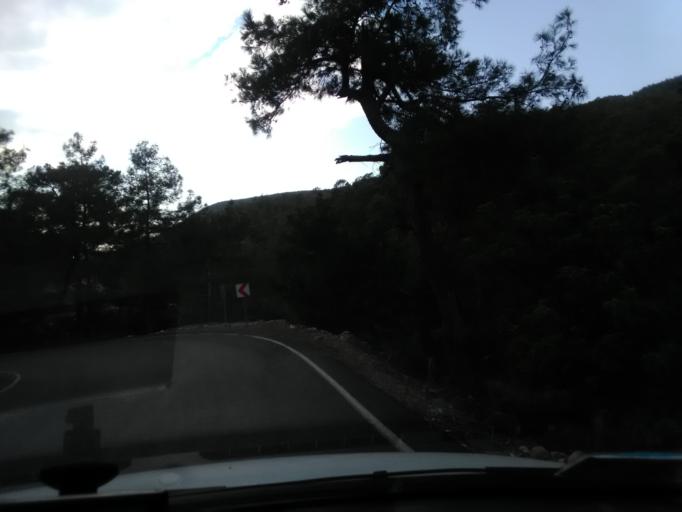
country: TR
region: Antalya
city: Gazipasa
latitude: 36.2890
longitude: 32.3769
